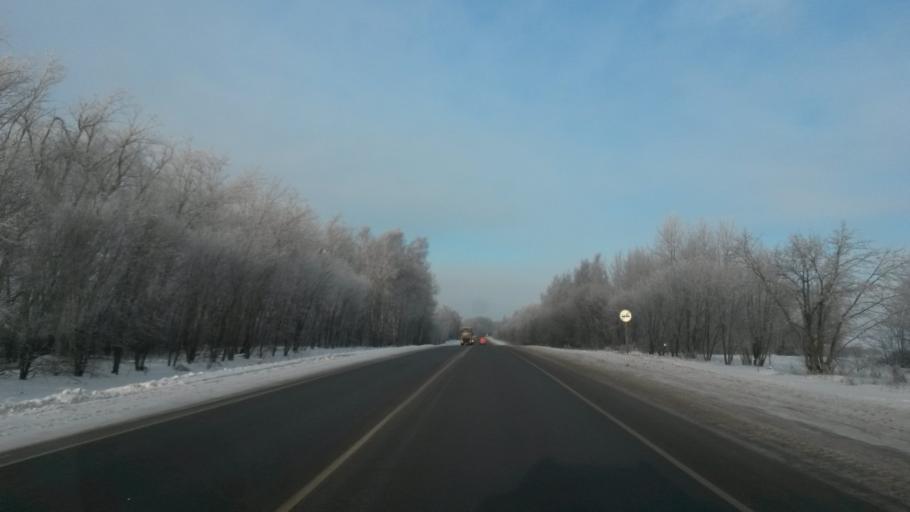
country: RU
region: Vladimir
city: Bogolyubovo
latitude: 56.2037
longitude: 40.4444
